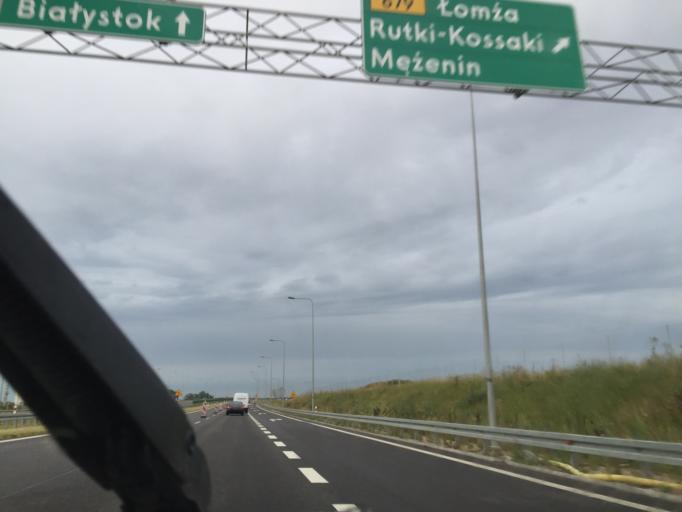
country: PL
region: Podlasie
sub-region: Powiat zambrowski
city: Rutki-Kossaki
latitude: 53.0903
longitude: 22.4918
